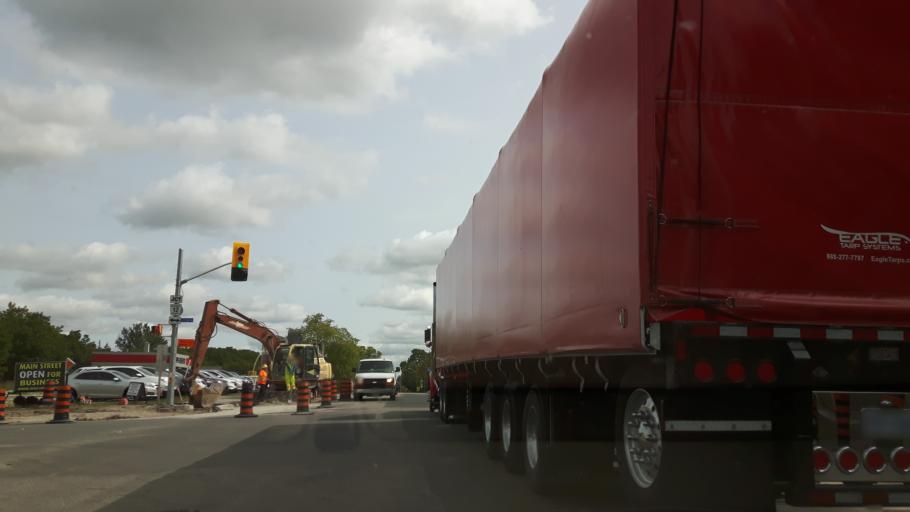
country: CA
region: Ontario
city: Huron East
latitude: 43.5534
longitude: -81.3936
